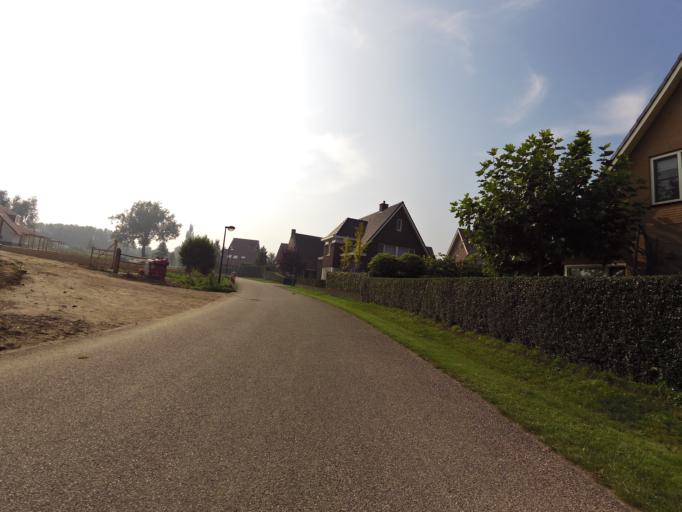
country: NL
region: Gelderland
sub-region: Gemeente Doetinchem
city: Doetinchem
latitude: 51.9487
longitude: 6.2653
